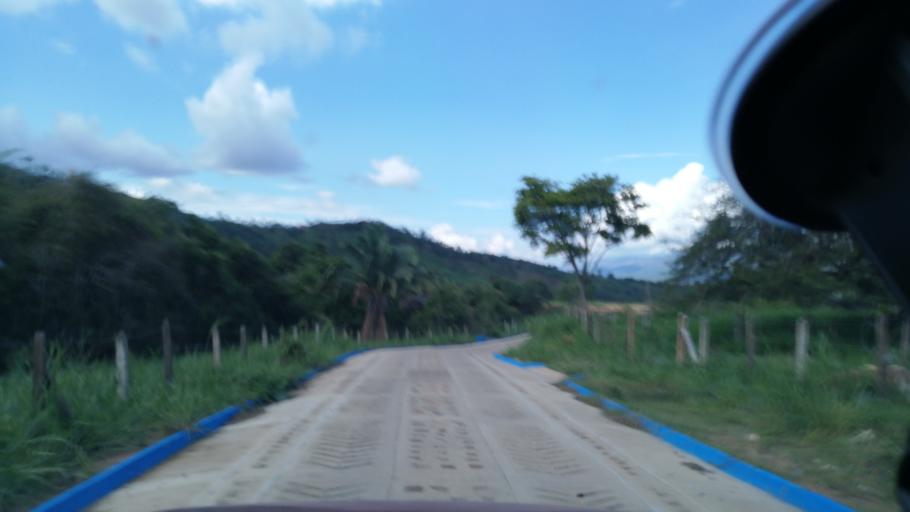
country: CO
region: Cundinamarca
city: Quipile
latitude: 4.7748
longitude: -74.6160
